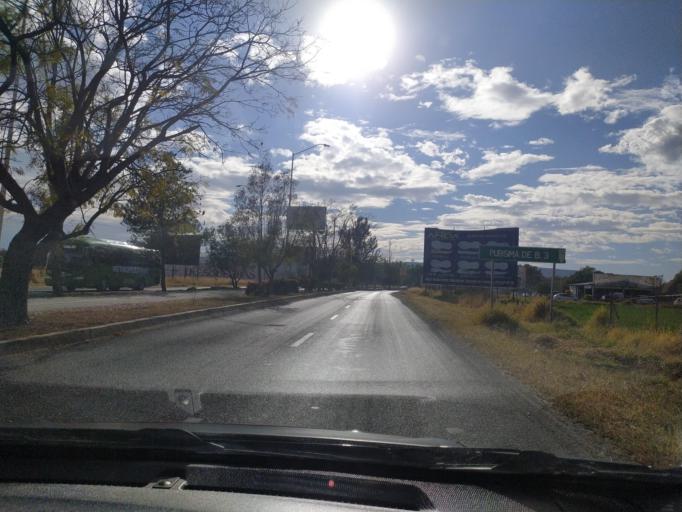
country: LA
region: Oudomxai
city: Muang La
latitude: 21.0319
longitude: 101.8308
